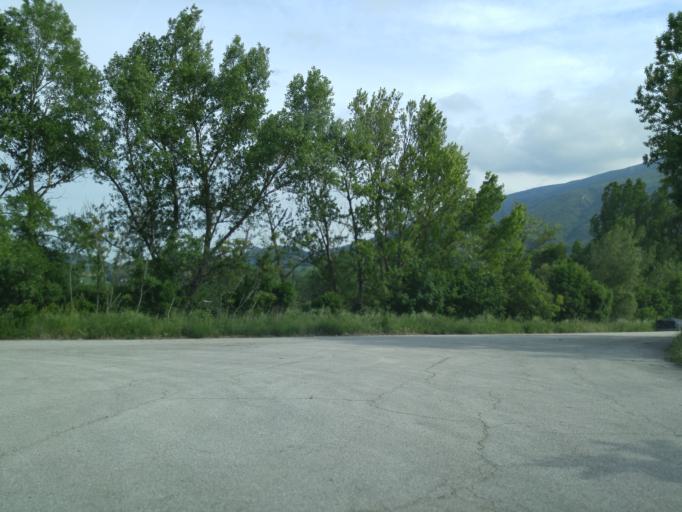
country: IT
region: The Marches
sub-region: Provincia di Pesaro e Urbino
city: Fossombrone
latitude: 43.6769
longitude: 12.7557
